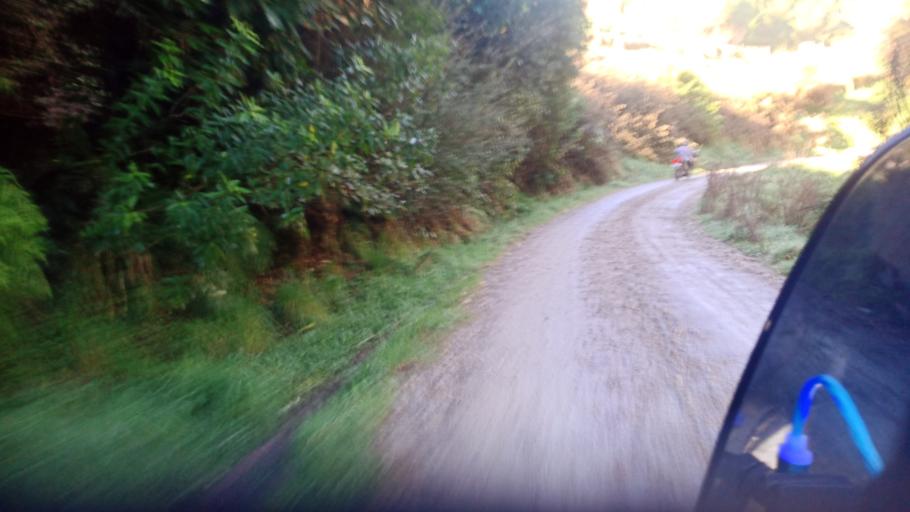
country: NZ
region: Hawke's Bay
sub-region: Wairoa District
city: Wairoa
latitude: -38.6671
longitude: 177.5416
